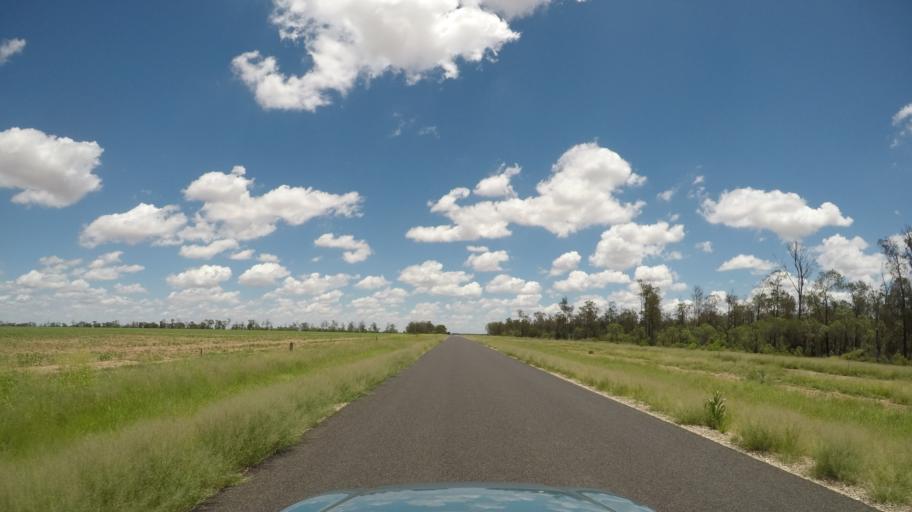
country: AU
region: Queensland
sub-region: Goondiwindi
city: Goondiwindi
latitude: -28.1731
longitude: 150.2347
